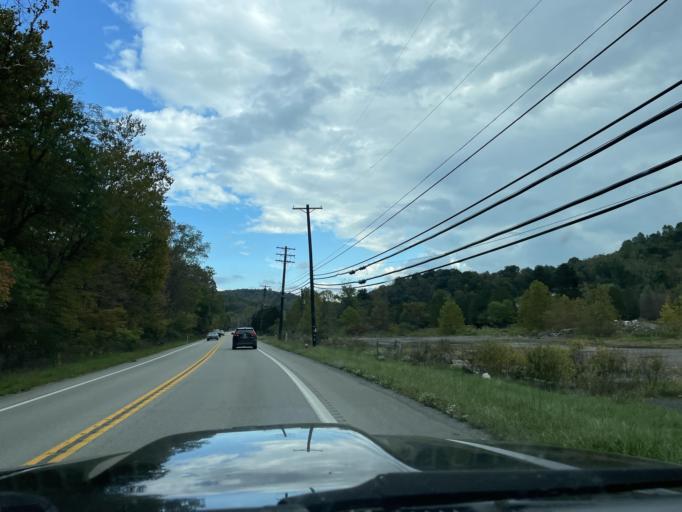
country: US
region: Pennsylvania
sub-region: Westmoreland County
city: Lower Burrell
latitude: 40.5435
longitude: -79.7292
